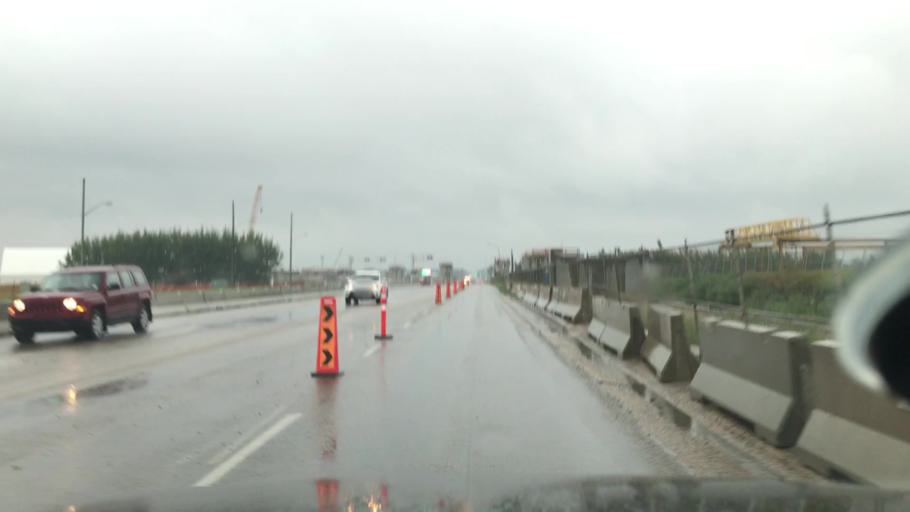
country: CA
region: Alberta
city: Edmonton
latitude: 53.4959
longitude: -113.4426
